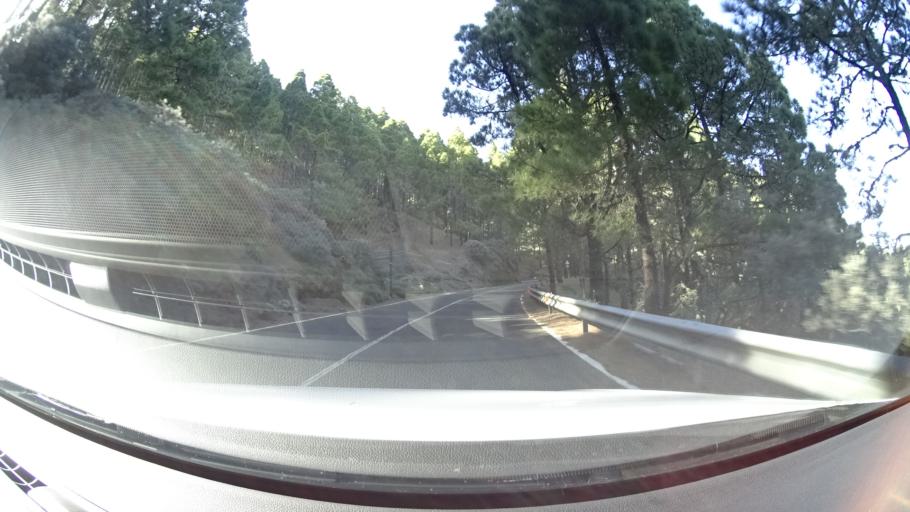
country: ES
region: Canary Islands
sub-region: Provincia de Las Palmas
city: Valsequillo de Gran Canaria
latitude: 27.9613
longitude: -15.5376
